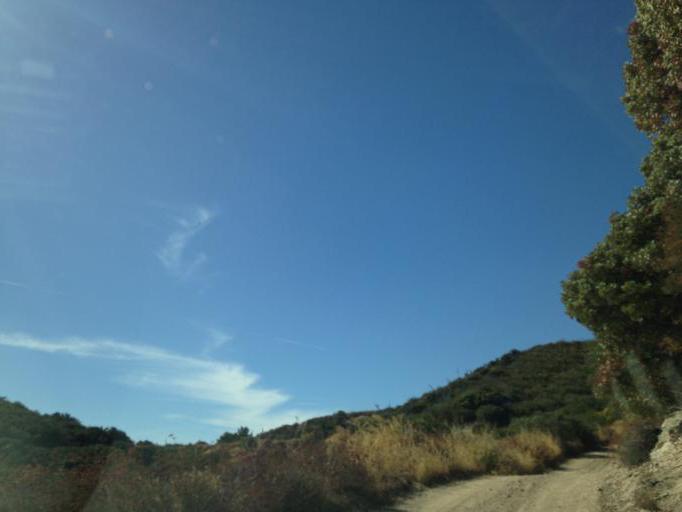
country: US
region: California
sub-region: San Bernardino County
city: Running Springs
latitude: 34.1702
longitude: -117.0927
